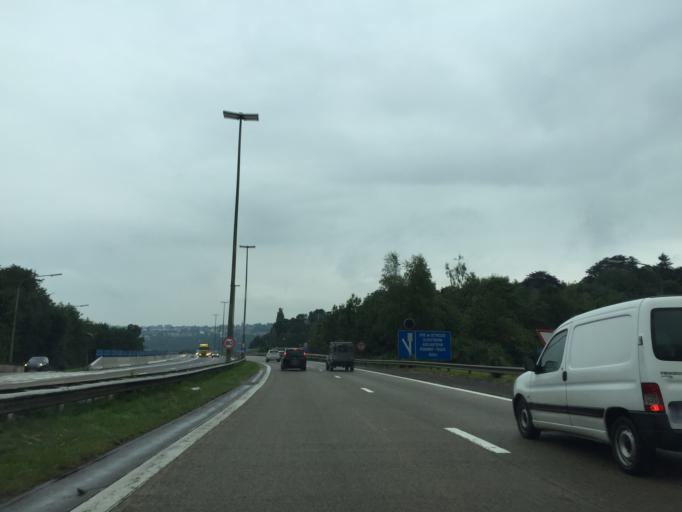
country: BE
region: Wallonia
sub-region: Province de Liege
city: Verviers
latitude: 50.5783
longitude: 5.8556
